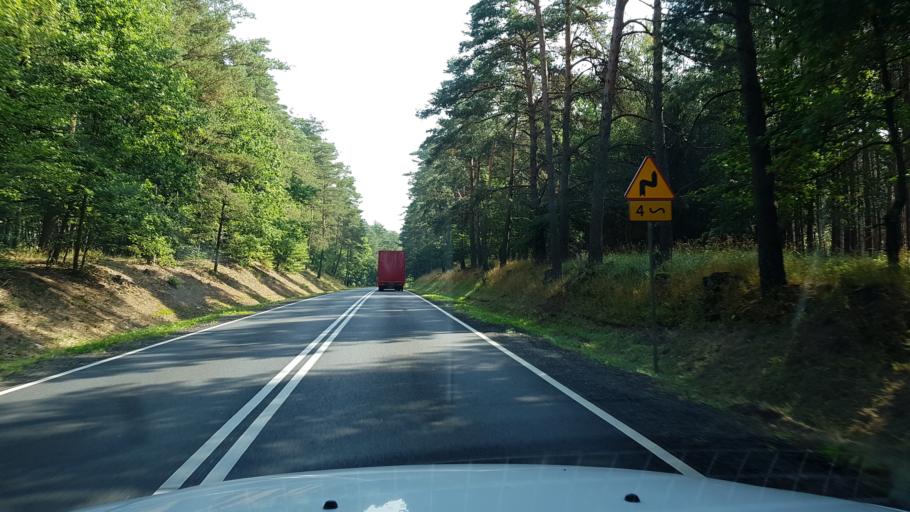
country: PL
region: West Pomeranian Voivodeship
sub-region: Powiat choszczenski
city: Drawno
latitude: 53.2972
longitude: 15.7409
